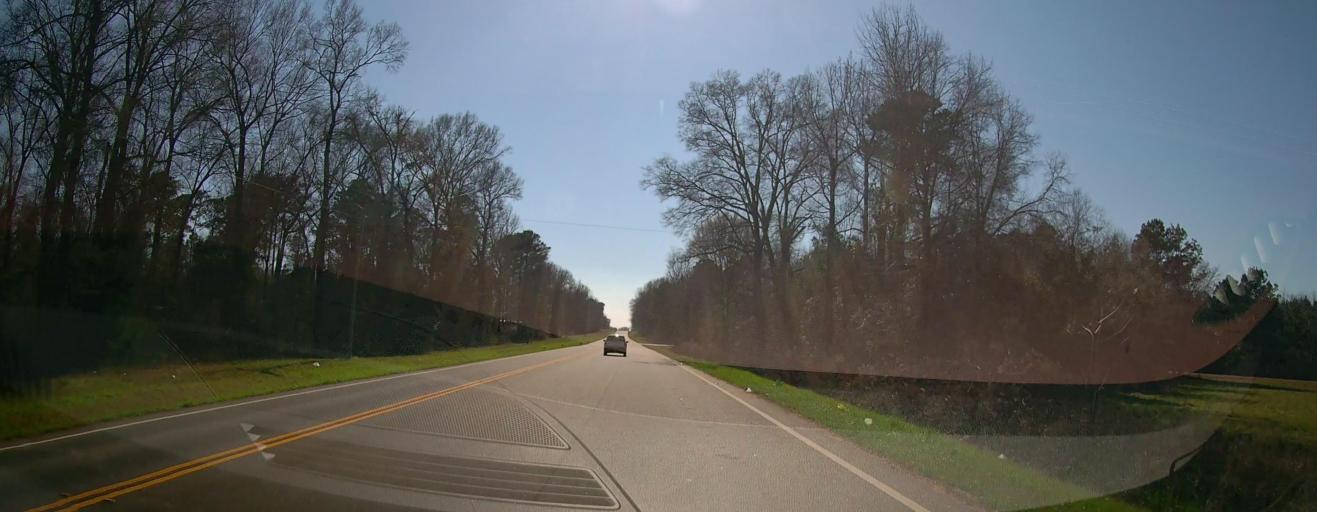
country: US
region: Georgia
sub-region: Macon County
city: Montezuma
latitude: 32.3177
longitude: -83.8938
